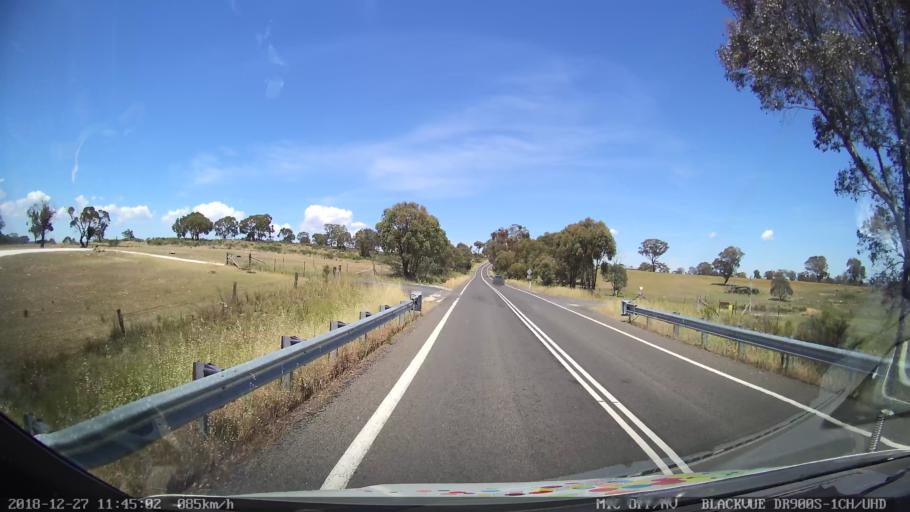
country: AU
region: New South Wales
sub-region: Bathurst Regional
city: Perthville
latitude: -33.5790
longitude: 149.4746
